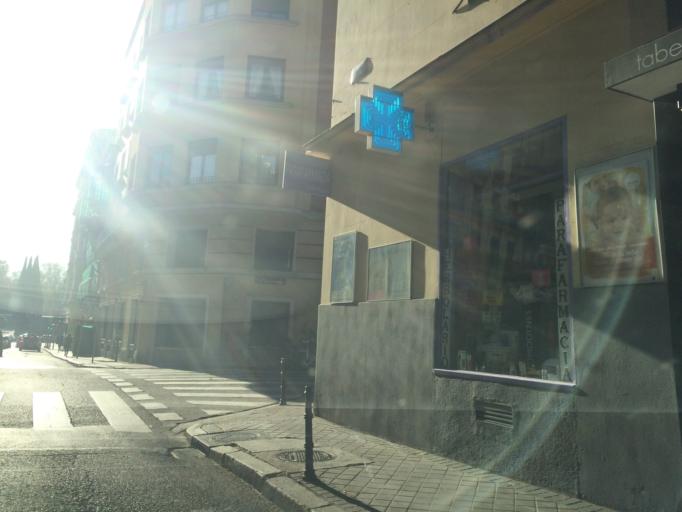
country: ES
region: Madrid
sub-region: Provincia de Madrid
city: Chamberi
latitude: 40.4256
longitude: -3.7152
